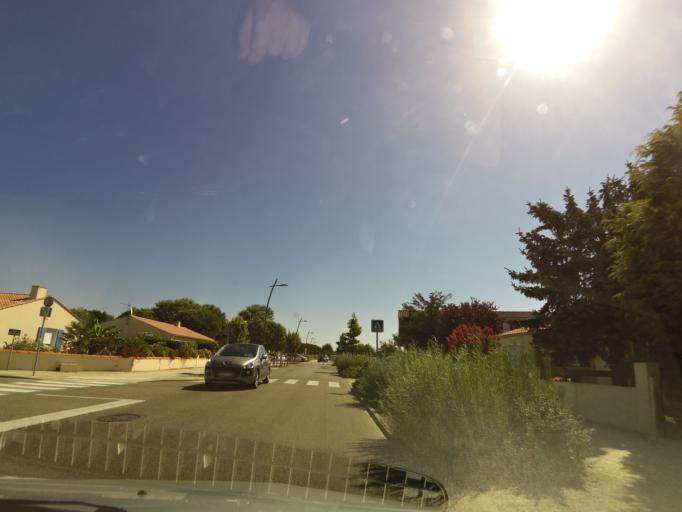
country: FR
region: Pays de la Loire
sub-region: Departement de la Vendee
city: Jard-sur-Mer
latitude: 46.4203
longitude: -1.5797
